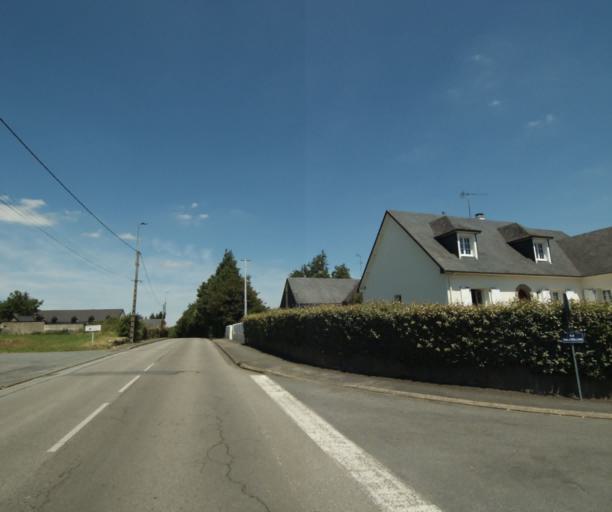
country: FR
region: Pays de la Loire
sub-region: Departement de la Mayenne
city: Laval
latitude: 48.0655
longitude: -0.7948
